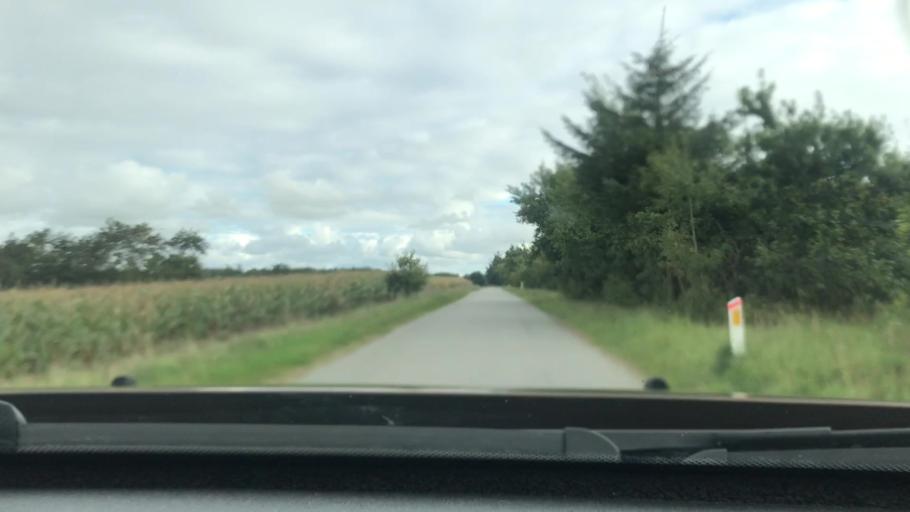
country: DK
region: South Denmark
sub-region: Esbjerg Kommune
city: Ribe
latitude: 55.3011
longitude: 8.7207
